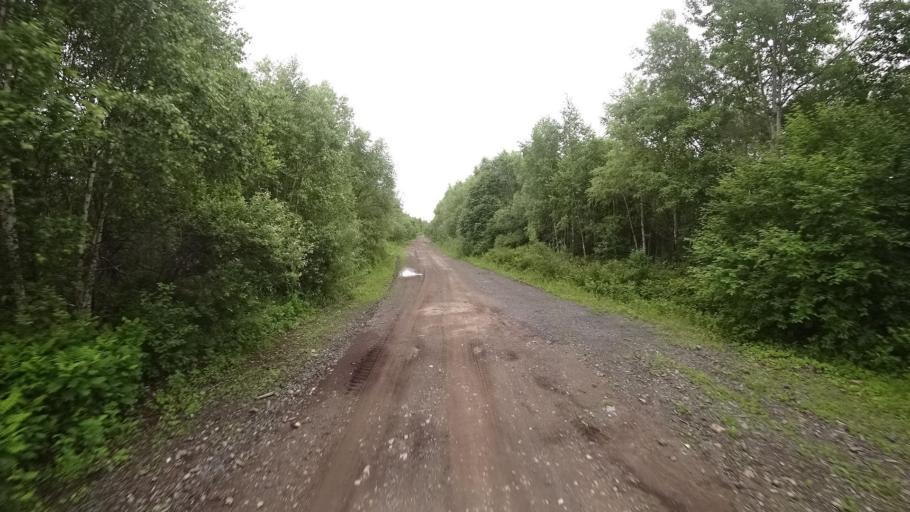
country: RU
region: Khabarovsk Krai
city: Amursk
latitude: 49.9125
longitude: 136.1583
